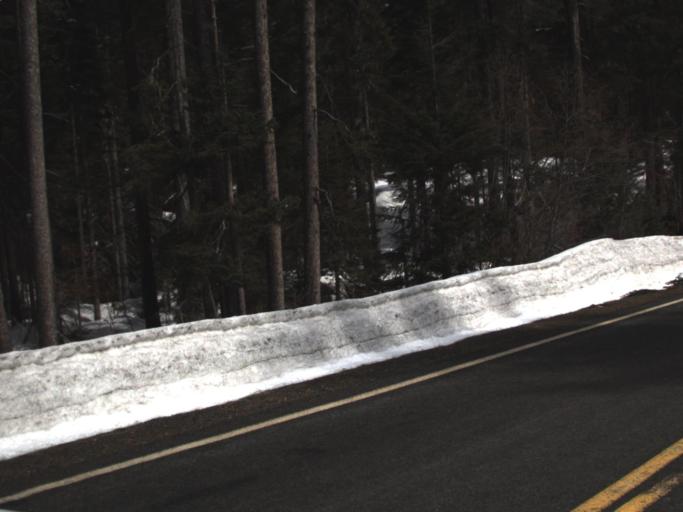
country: US
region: Washington
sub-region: Kittitas County
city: Cle Elum
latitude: 46.9147
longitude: -121.3916
